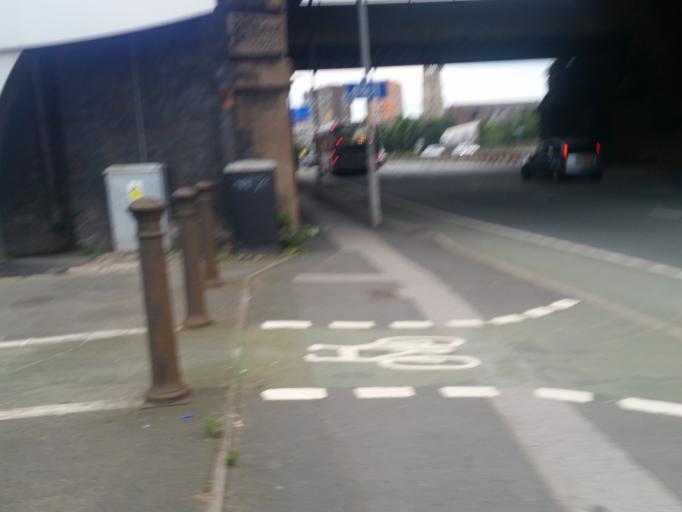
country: GB
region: England
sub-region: Manchester
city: Hulme
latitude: 53.4743
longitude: -2.2606
